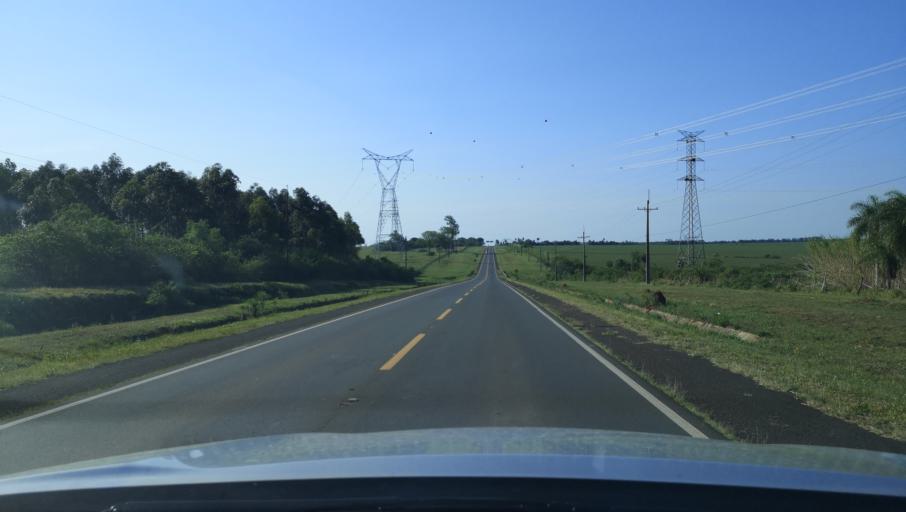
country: PY
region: Misiones
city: Santa Maria
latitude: -26.7913
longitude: -57.0245
